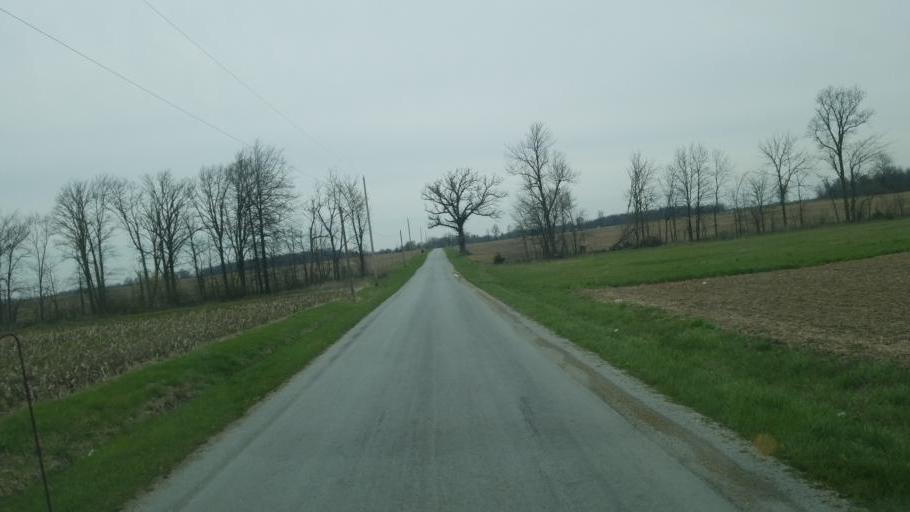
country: US
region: Ohio
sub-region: Hardin County
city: Forest
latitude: 40.8184
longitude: -83.4922
